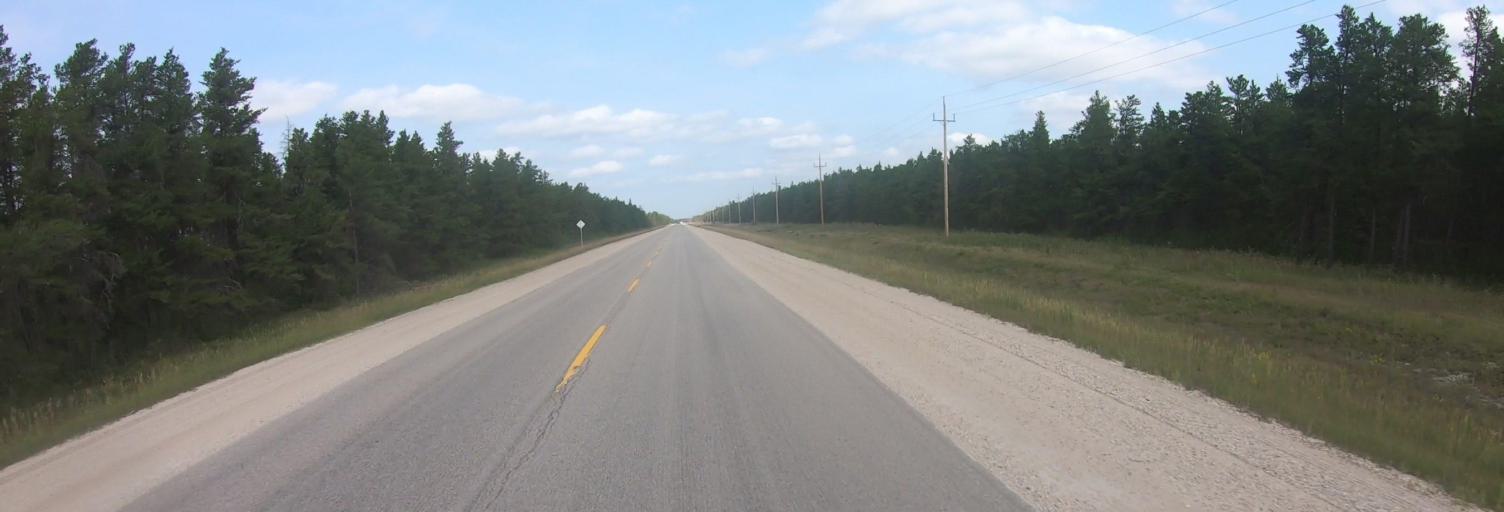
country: CA
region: Manitoba
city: La Broquerie
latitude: 49.2409
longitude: -96.3458
